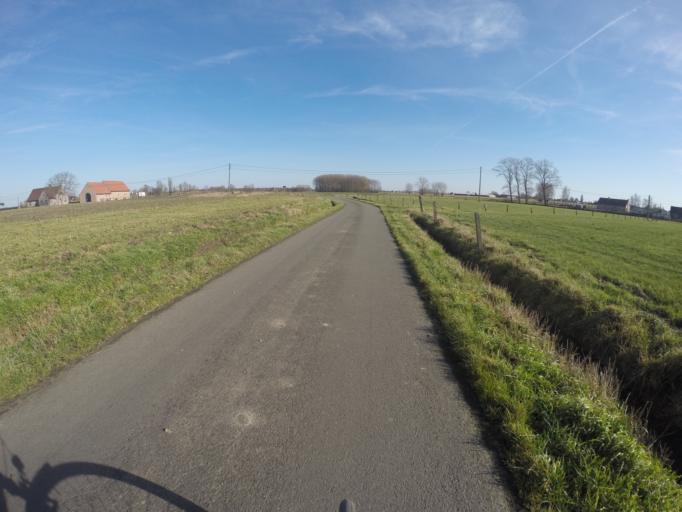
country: BE
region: Flanders
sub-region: Provincie West-Vlaanderen
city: Ruiselede
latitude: 51.0417
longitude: 3.4203
